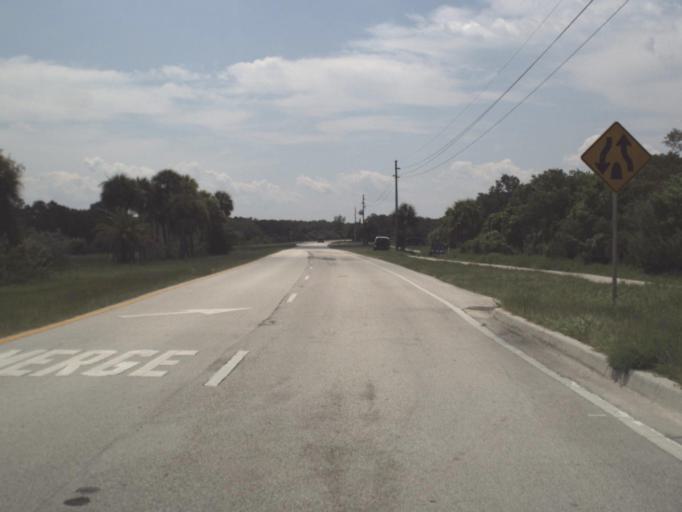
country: US
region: Florida
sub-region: Pinellas County
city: Tierra Verde
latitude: 27.6602
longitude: -82.7225
